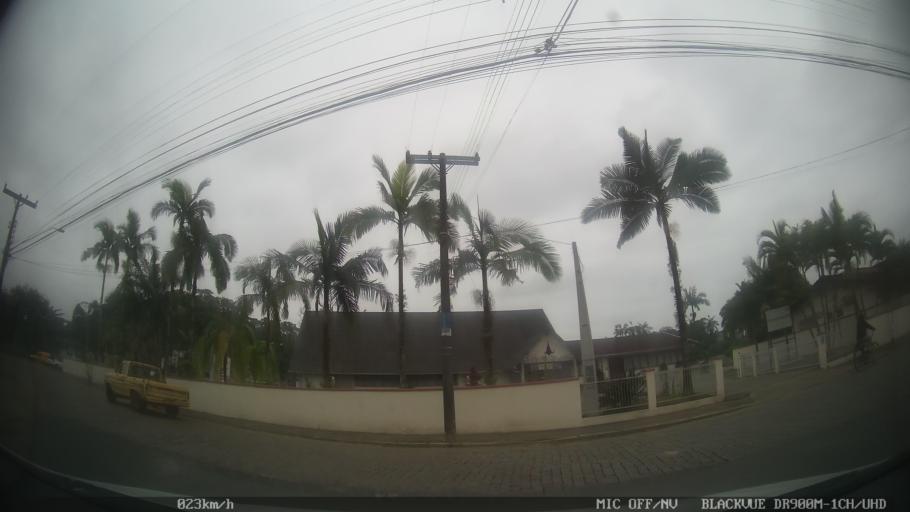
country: BR
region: Santa Catarina
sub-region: Joinville
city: Joinville
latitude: -26.3308
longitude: -48.8498
